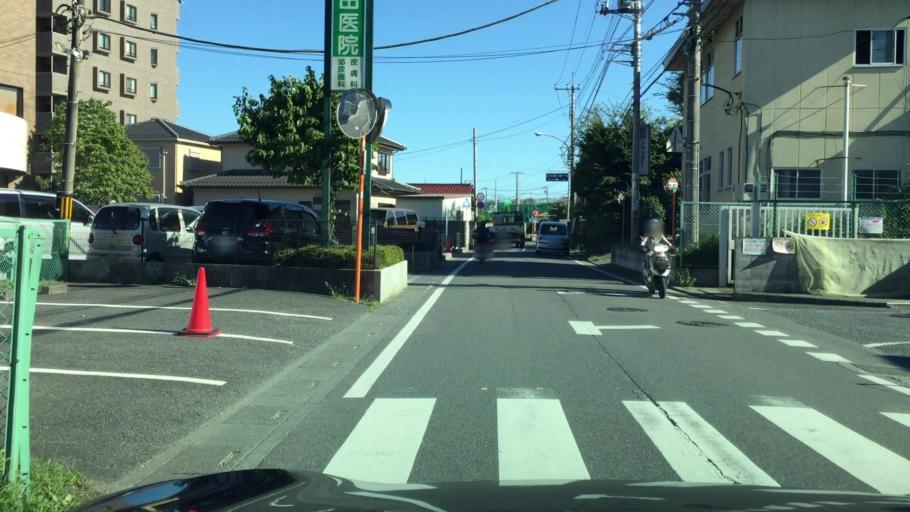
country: JP
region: Saitama
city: Ageoshimo
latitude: 35.9224
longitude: 139.5854
